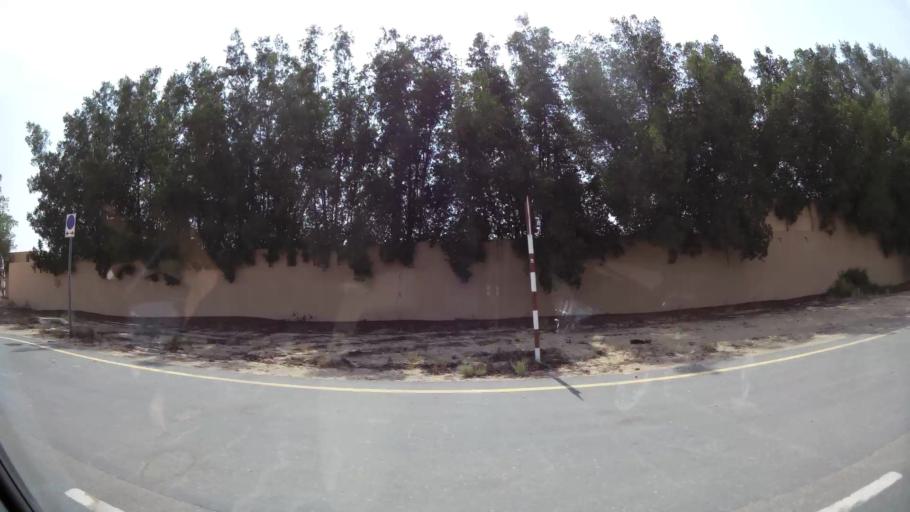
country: AE
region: Ash Shariqah
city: Sharjah
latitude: 25.2427
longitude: 55.4800
